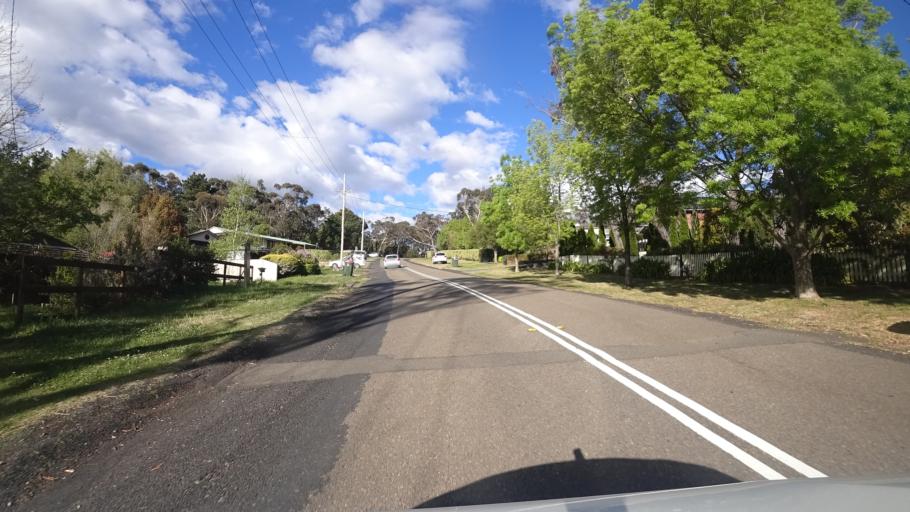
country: AU
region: New South Wales
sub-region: Blue Mountains Municipality
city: Katoomba
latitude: -33.7207
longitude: 150.2923
